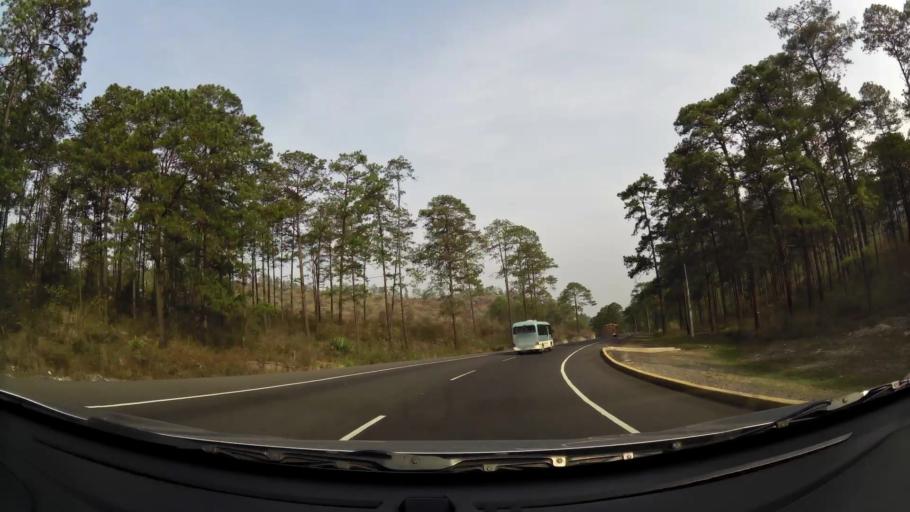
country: HN
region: Francisco Morazan
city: Zambrano
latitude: 14.2865
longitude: -87.4735
